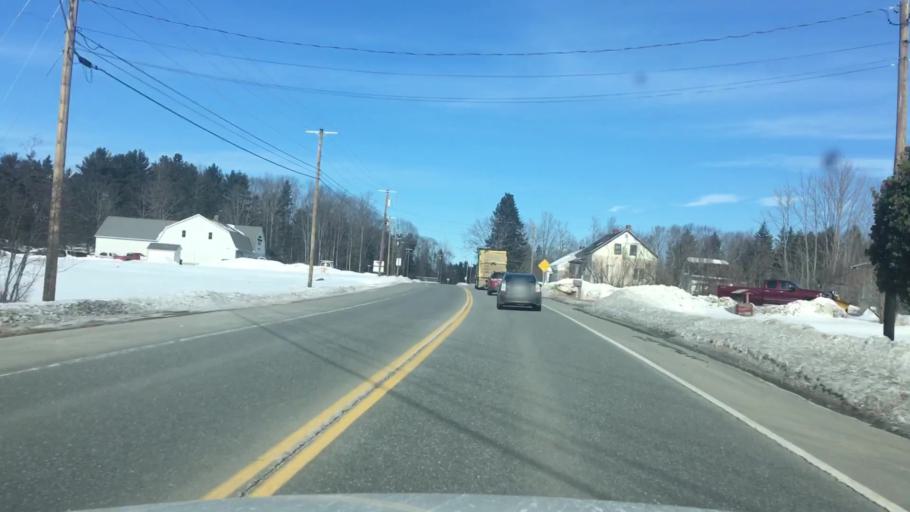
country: US
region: Maine
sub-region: Penobscot County
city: Orrington
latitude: 44.7356
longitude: -68.8218
